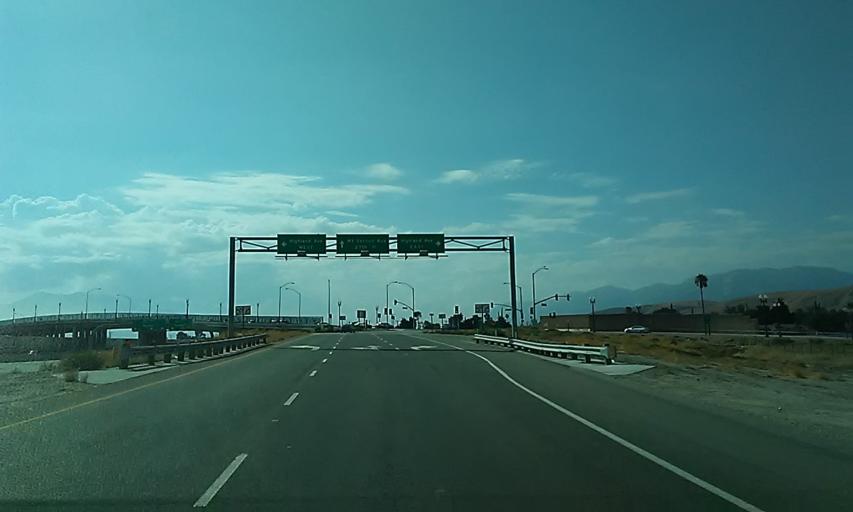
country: US
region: California
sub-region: San Bernardino County
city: San Bernardino
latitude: 34.1349
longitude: -117.3104
